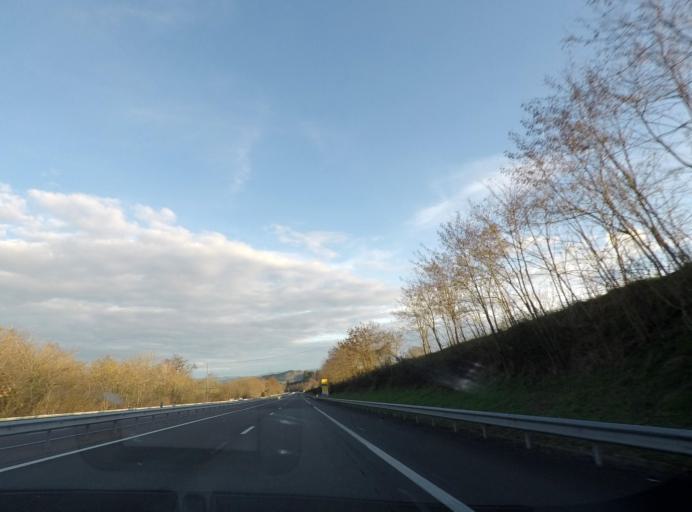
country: FR
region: Bourgogne
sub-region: Departement de Saone-et-Loire
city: Matour
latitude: 46.3843
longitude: 4.4677
